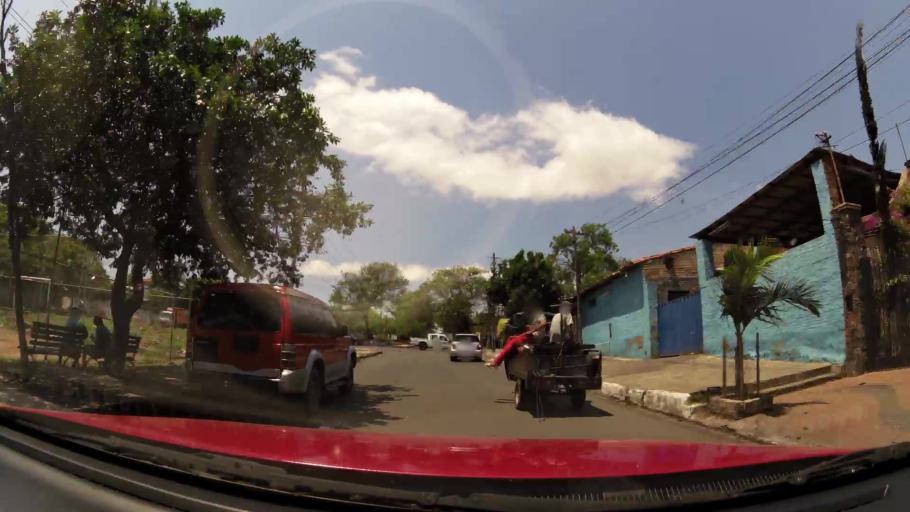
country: PY
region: Asuncion
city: Asuncion
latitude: -25.3073
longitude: -57.6442
